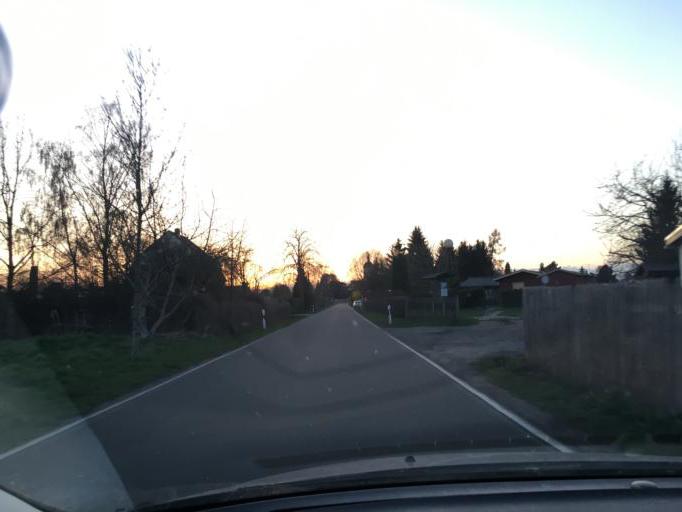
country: DE
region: Saxony
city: Borsdorf
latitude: 51.3335
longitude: 12.4949
